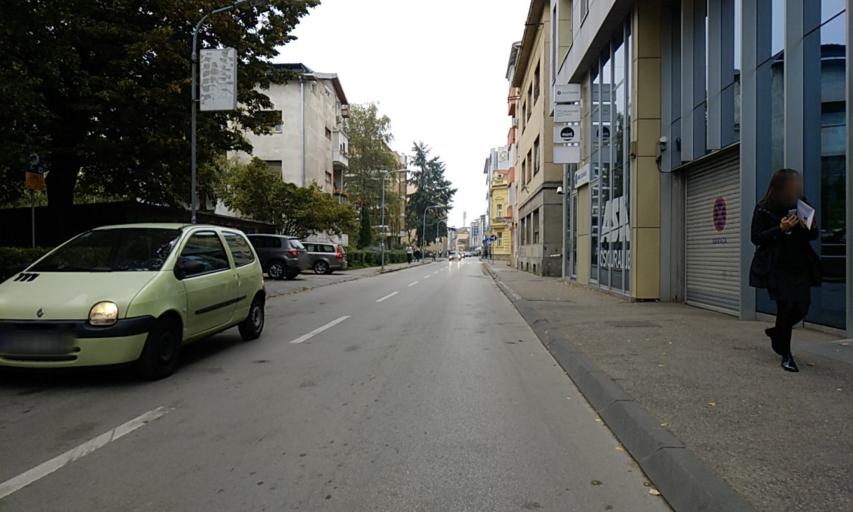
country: BA
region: Republika Srpska
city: Mejdan - Obilicevo
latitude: 44.7692
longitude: 17.1945
